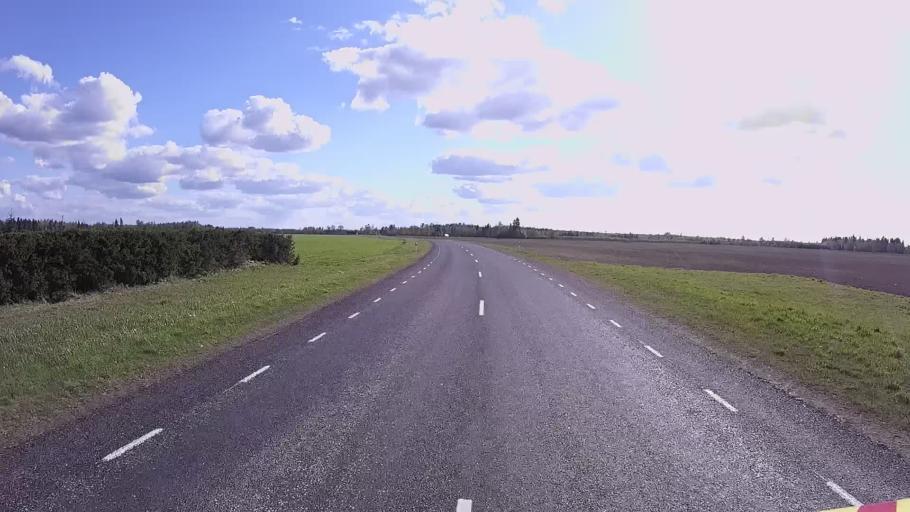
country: EE
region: Jogevamaa
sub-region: Jogeva linn
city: Jogeva
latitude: 58.7263
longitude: 26.1939
